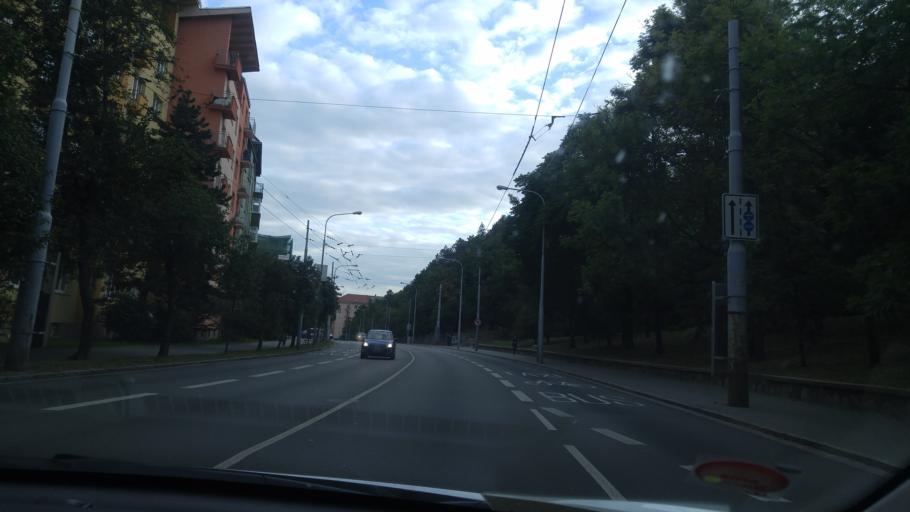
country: CZ
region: South Moravian
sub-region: Mesto Brno
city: Brno
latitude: 49.2030
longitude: 16.5927
